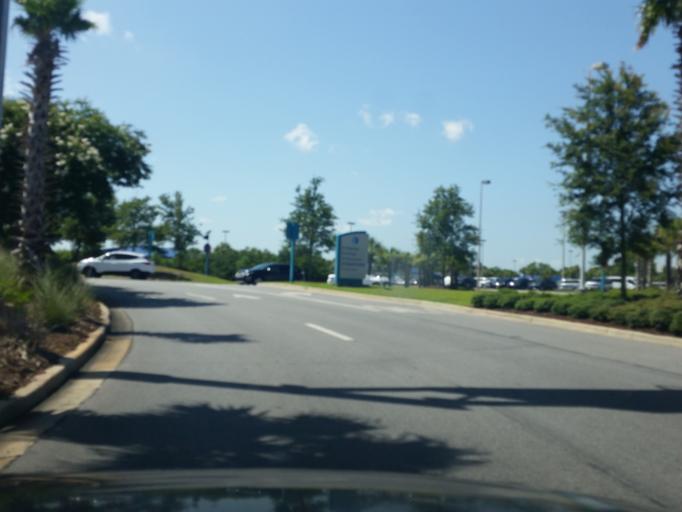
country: US
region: Florida
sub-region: Escambia County
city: Ferry Pass
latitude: 30.4777
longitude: -87.1936
